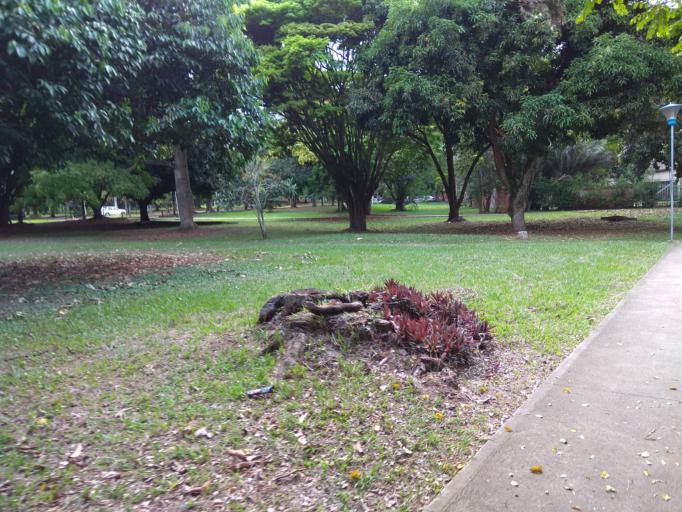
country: CO
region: Valle del Cauca
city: Cali
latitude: 3.3740
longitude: -76.5321
